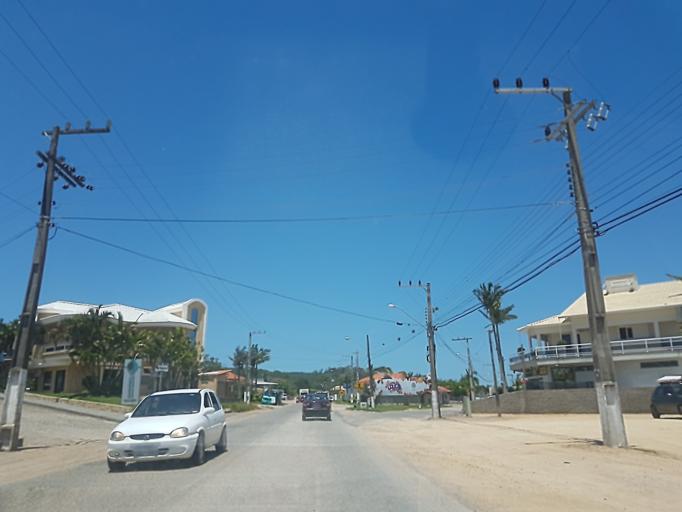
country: BR
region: Santa Catarina
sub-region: Jaguaruna
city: Jaguaruna
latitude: -28.6017
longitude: -49.0424
